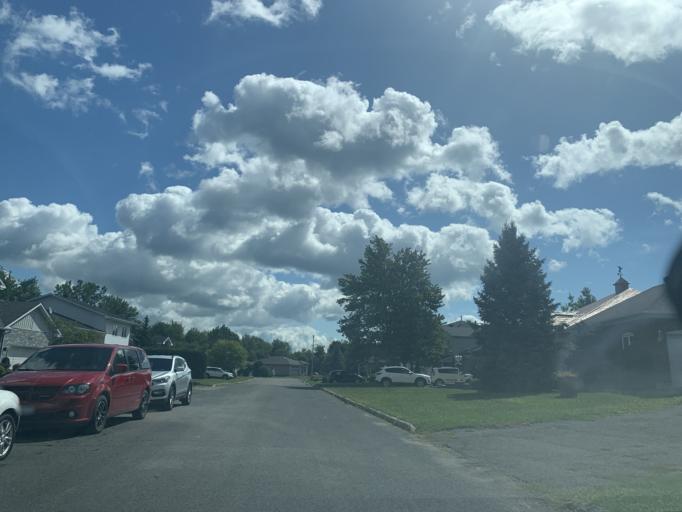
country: CA
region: Ontario
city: Hawkesbury
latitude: 45.6009
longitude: -74.6009
